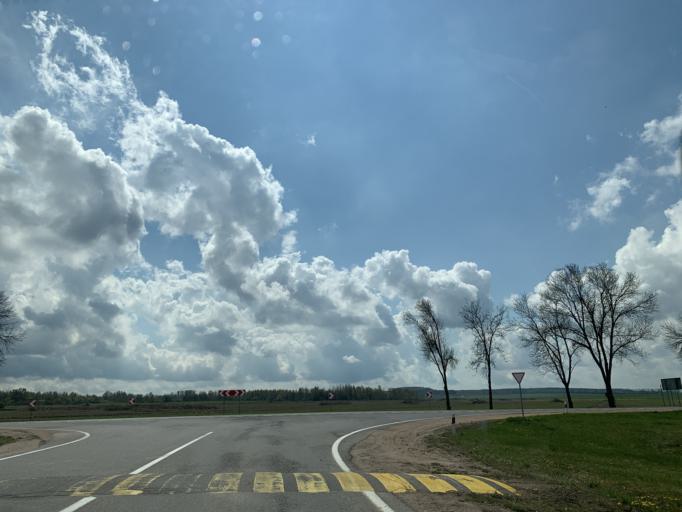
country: BY
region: Minsk
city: Nyasvizh
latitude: 53.2295
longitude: 26.7234
